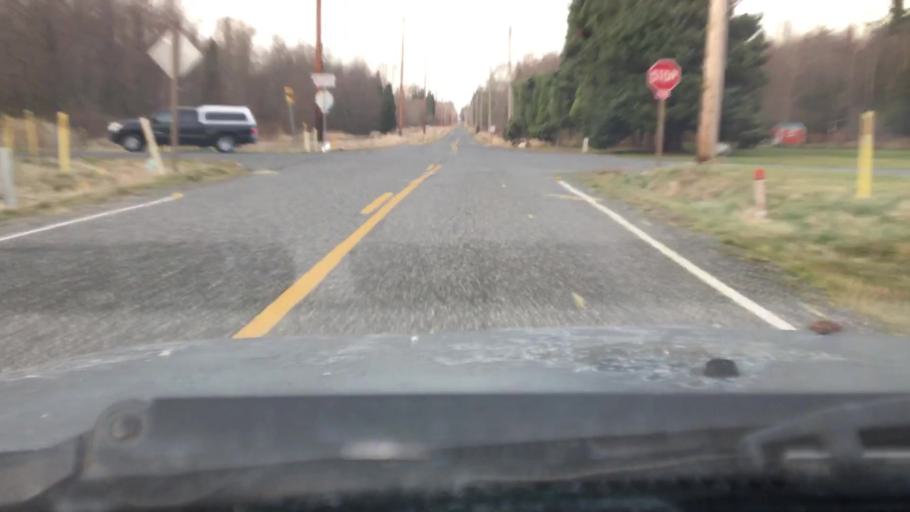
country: US
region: Washington
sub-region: Whatcom County
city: Birch Bay
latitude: 48.8628
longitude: -122.7043
